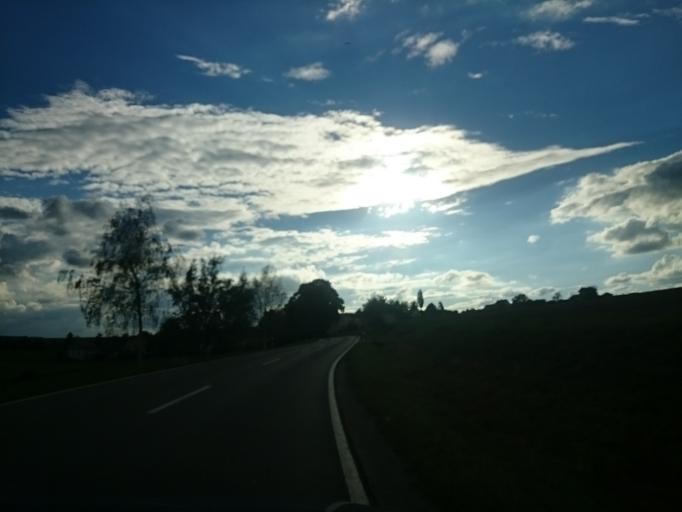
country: DE
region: Bavaria
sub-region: Regierungsbezirk Mittelfranken
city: Thalmassing
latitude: 49.1265
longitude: 11.1959
